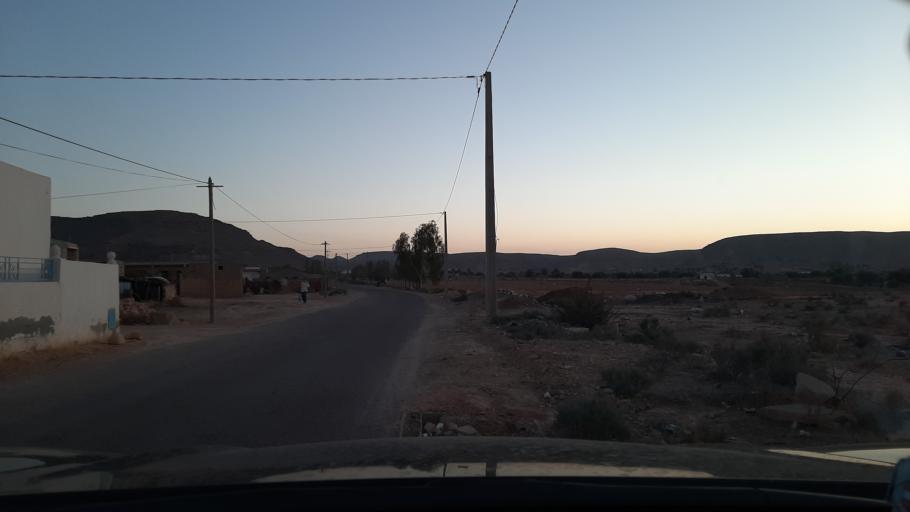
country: TN
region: Qabis
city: Matmata
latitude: 33.5708
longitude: 10.1787
